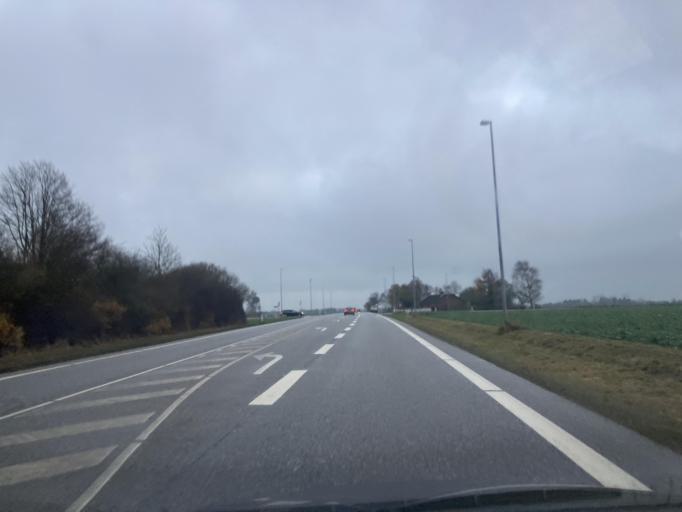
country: DK
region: Zealand
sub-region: Lolland Kommune
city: Holeby
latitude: 54.7095
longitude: 11.4546
